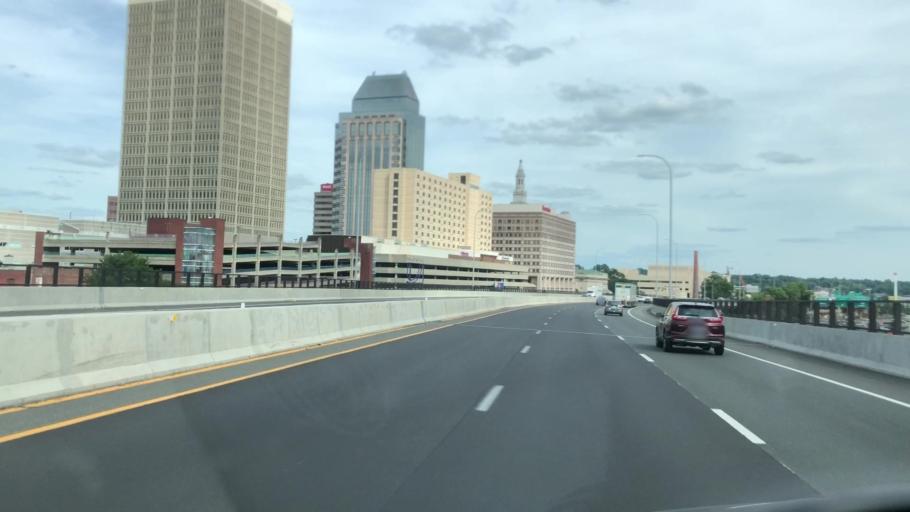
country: US
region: Massachusetts
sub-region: Hampden County
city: Springfield
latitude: 42.1029
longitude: -72.5957
